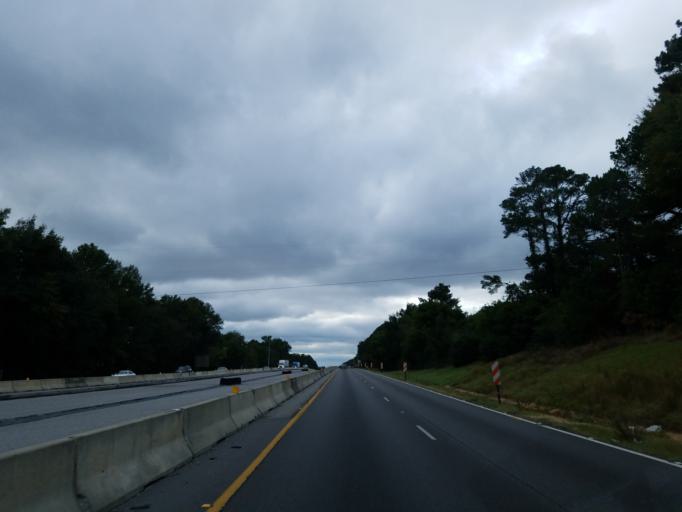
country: US
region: Alabama
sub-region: Tuscaloosa County
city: Holt
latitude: 33.1758
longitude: -87.4907
